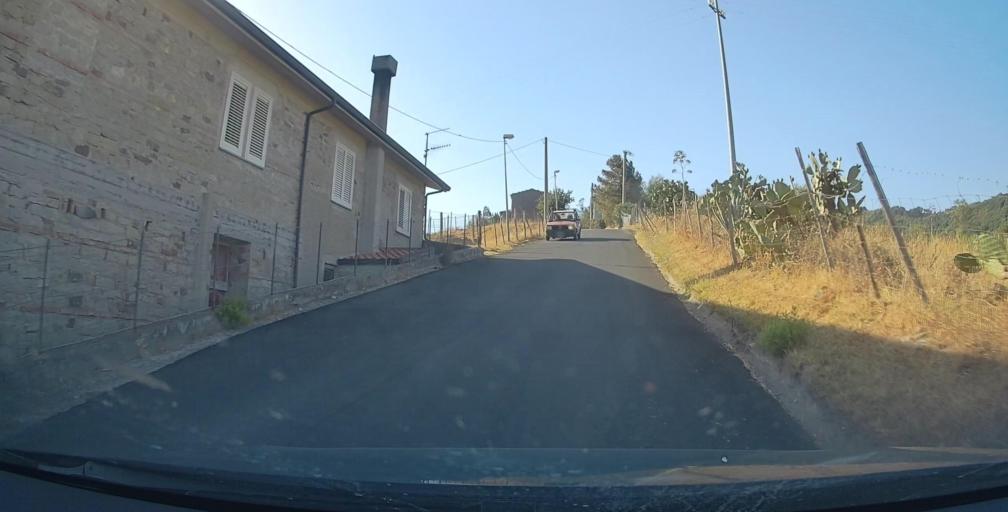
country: IT
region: Sicily
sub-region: Messina
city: San Piero Patti
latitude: 38.0599
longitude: 14.9924
